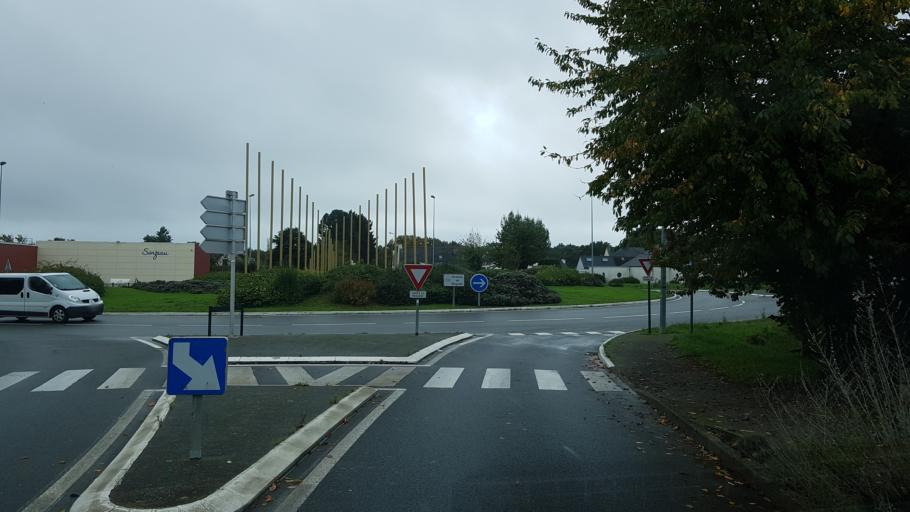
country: FR
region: Brittany
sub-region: Departement du Morbihan
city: Sarzeau
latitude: 47.5227
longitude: -2.7676
